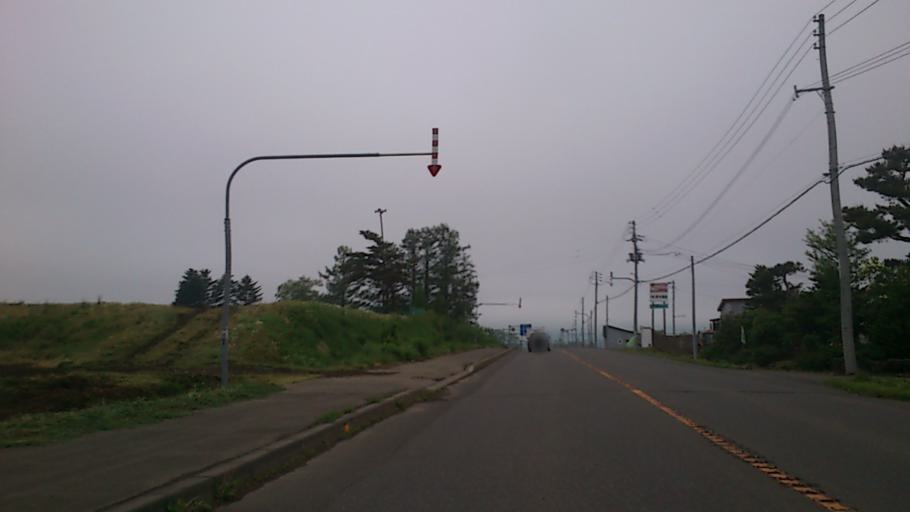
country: JP
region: Hokkaido
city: Niseko Town
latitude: 42.8829
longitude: 140.7760
